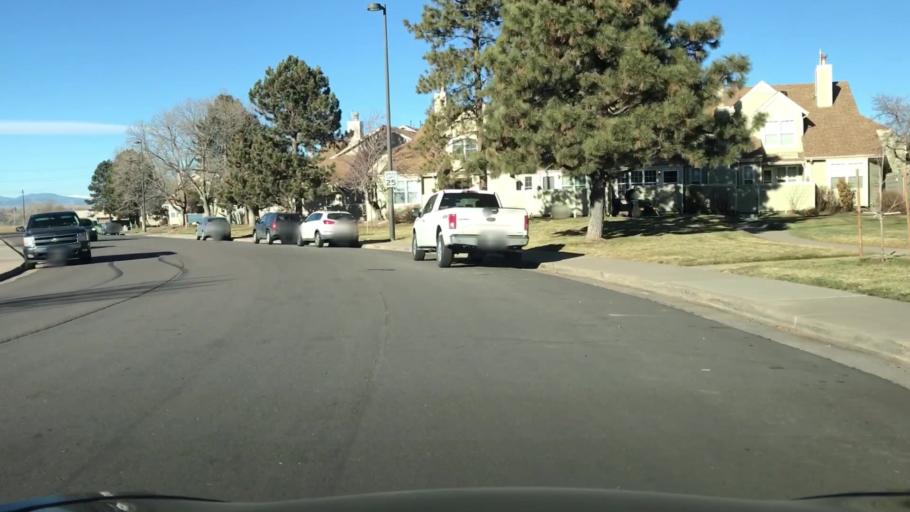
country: US
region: Colorado
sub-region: Arapahoe County
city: Glendale
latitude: 39.6873
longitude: -104.9013
